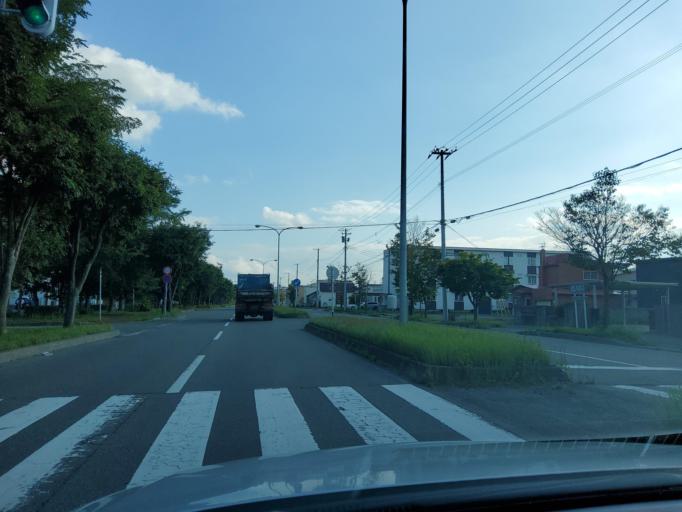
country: JP
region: Hokkaido
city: Obihiro
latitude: 42.9080
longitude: 143.2137
